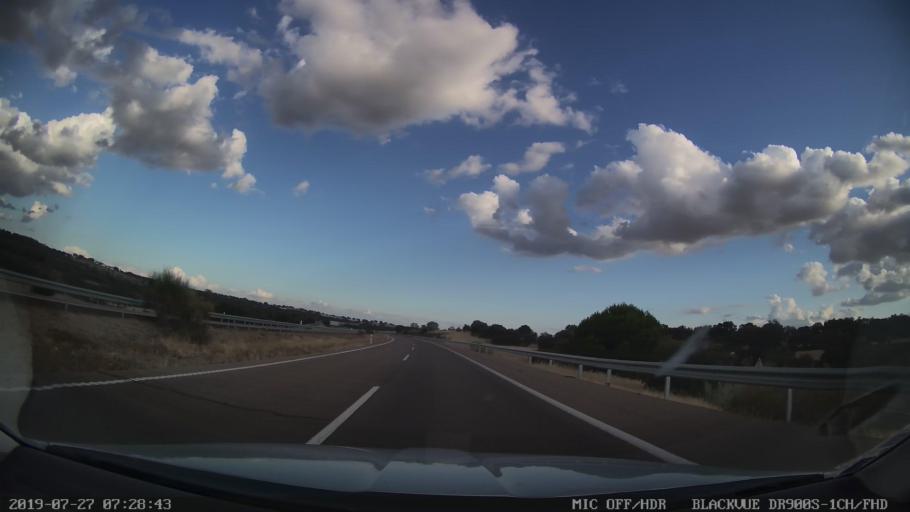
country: ES
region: Extremadura
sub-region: Provincia de Caceres
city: Villamesias
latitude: 39.2202
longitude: -5.8835
